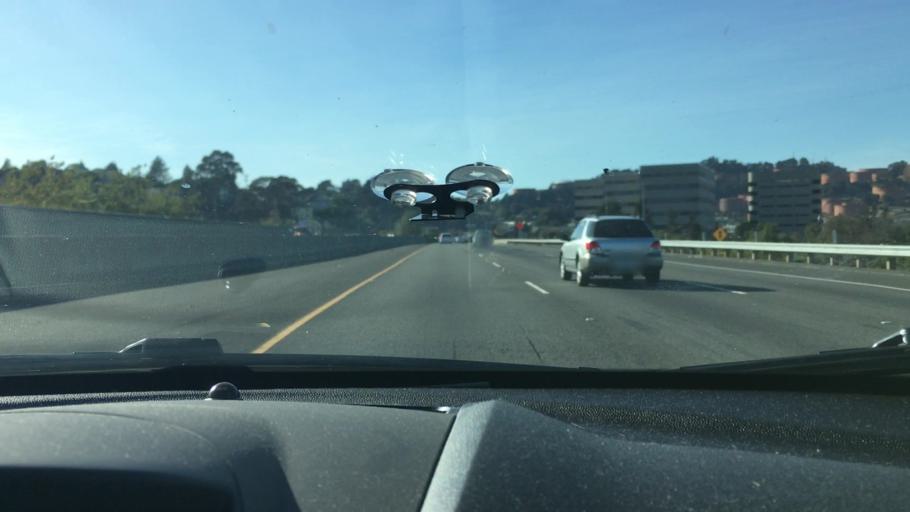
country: US
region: California
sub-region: Contra Costa County
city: North Richmond
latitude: 37.9285
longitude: -122.3840
